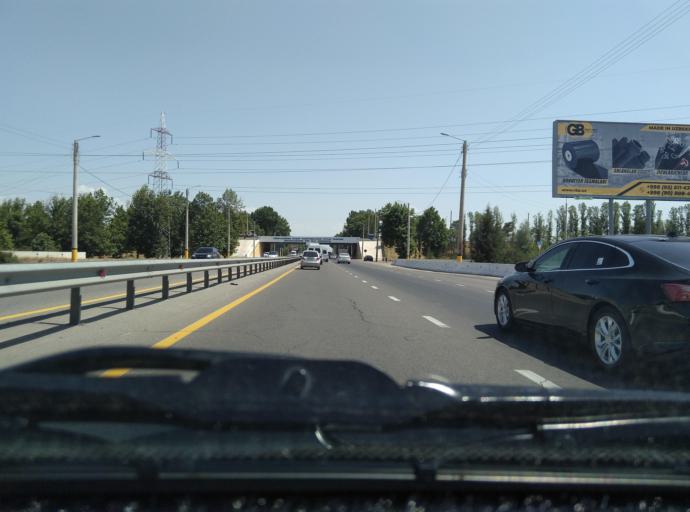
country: UZ
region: Toshkent Shahri
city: Bektemir
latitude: 41.2461
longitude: 69.3943
